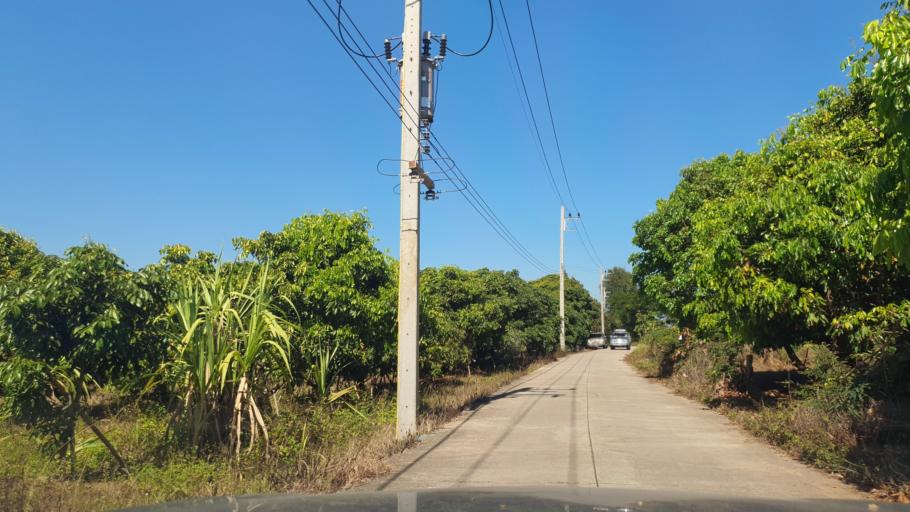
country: TH
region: Chiang Mai
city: Mae Wang
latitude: 18.6578
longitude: 98.8307
